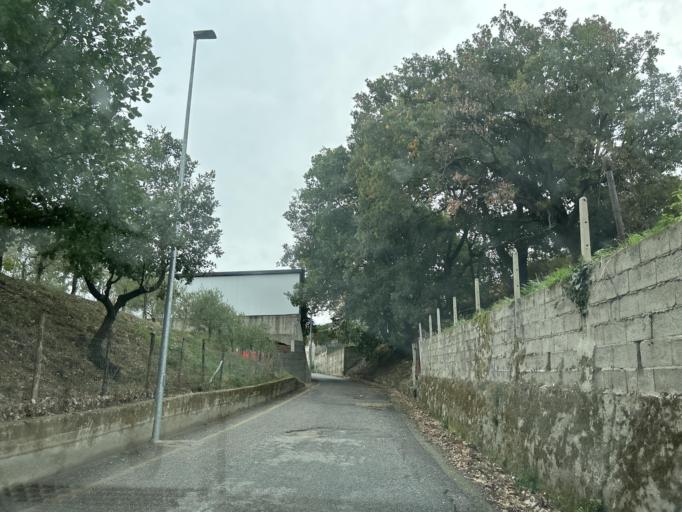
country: IT
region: Calabria
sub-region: Provincia di Catanzaro
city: Staletti
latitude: 38.7667
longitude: 16.5359
